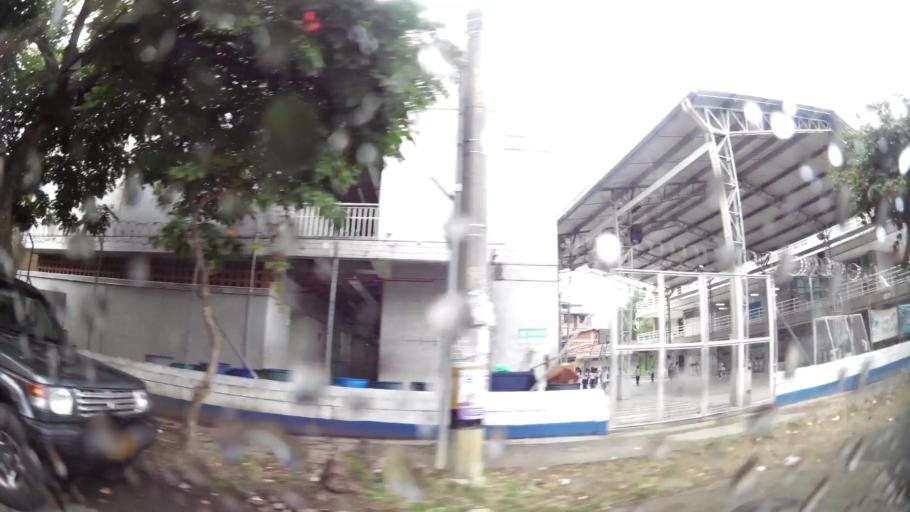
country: CO
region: Antioquia
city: Itagui
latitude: 6.1842
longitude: -75.5938
